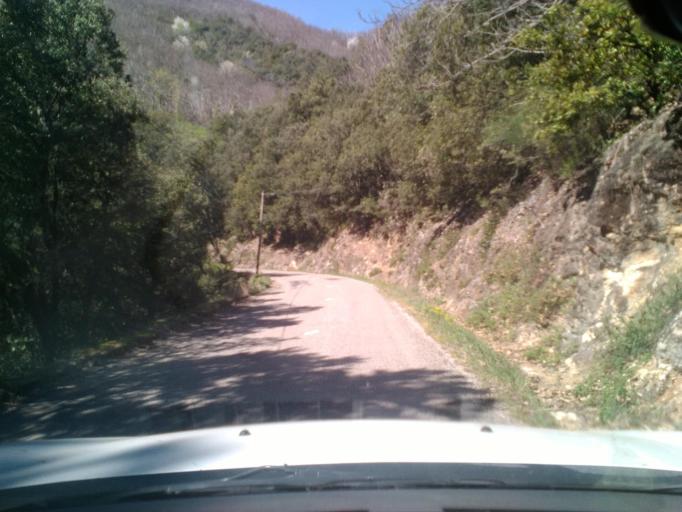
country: FR
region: Languedoc-Roussillon
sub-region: Departement du Gard
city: Lasalle
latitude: 44.0907
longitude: 3.8019
